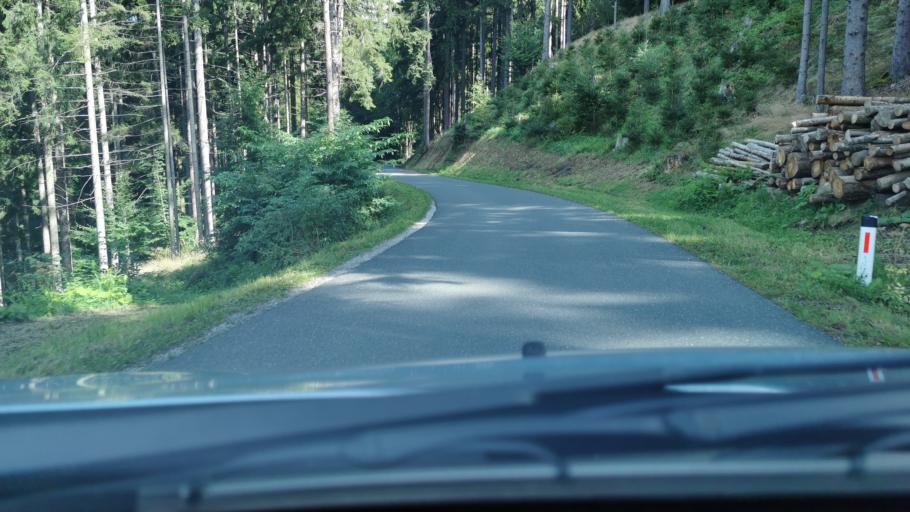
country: AT
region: Styria
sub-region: Politischer Bezirk Weiz
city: Koglhof
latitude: 47.3140
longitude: 15.7067
